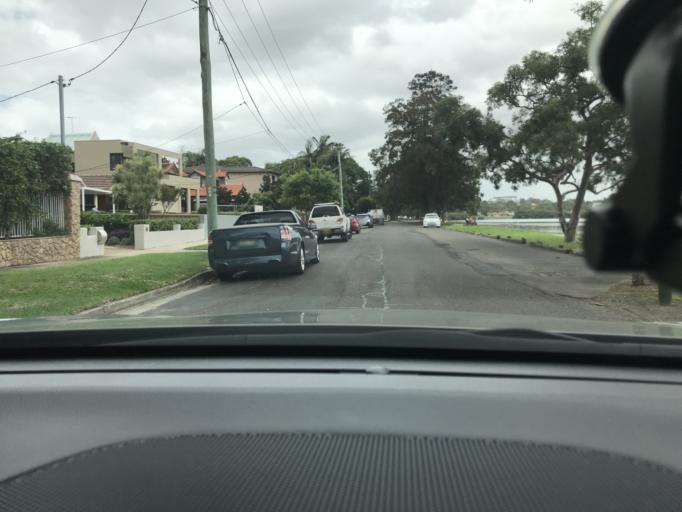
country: AU
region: New South Wales
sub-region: Canada Bay
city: Wareemba
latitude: -33.8563
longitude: 151.1277
